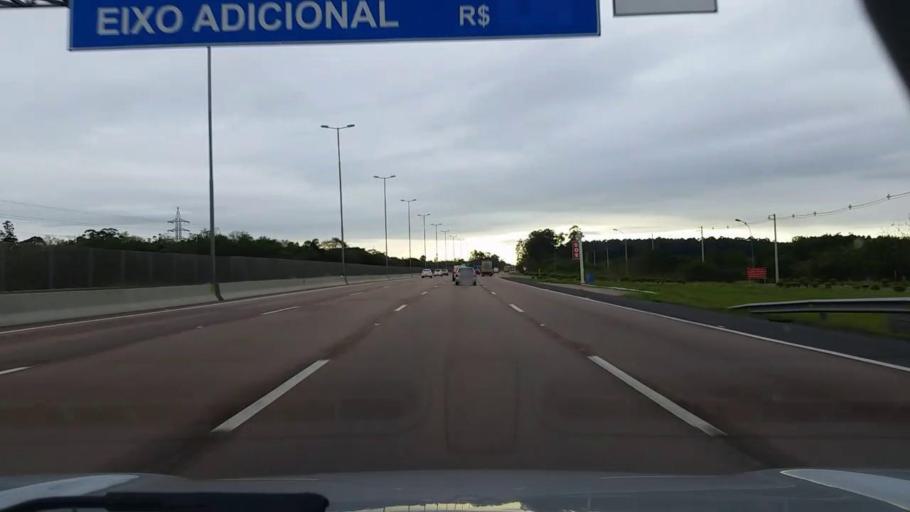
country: BR
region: Rio Grande do Sul
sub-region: Cachoeirinha
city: Cachoeirinha
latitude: -29.9531
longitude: -51.0499
